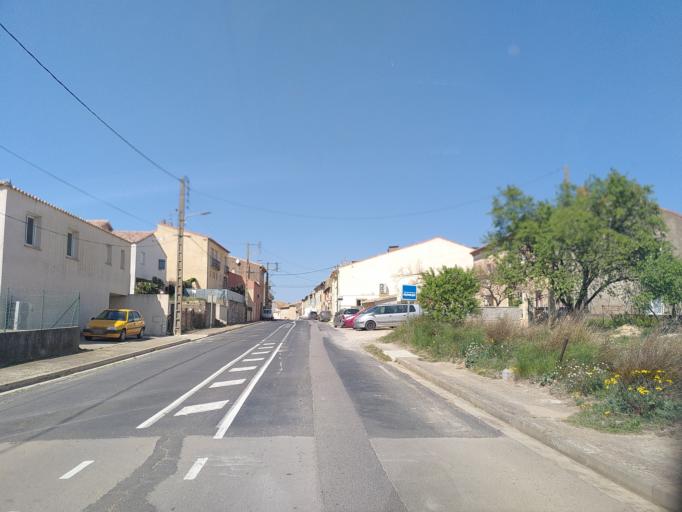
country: FR
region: Languedoc-Roussillon
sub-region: Departement de l'Aude
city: Ferrals-les-Corbieres
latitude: 43.1021
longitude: 2.7737
